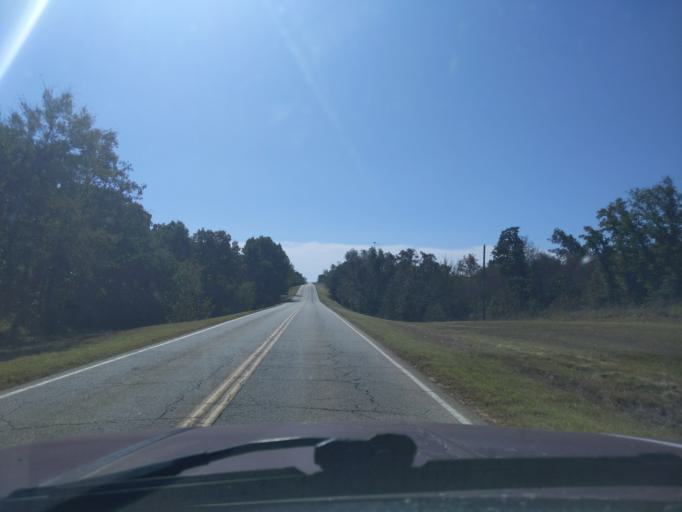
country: US
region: Oklahoma
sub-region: Creek County
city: Bristow
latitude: 35.7314
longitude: -96.3872
